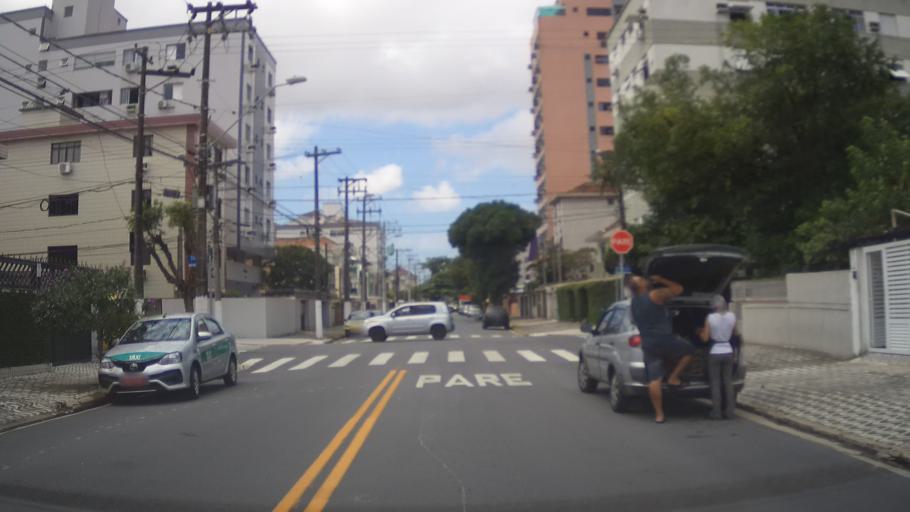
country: BR
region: Sao Paulo
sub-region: Santos
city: Santos
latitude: -23.9753
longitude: -46.3011
